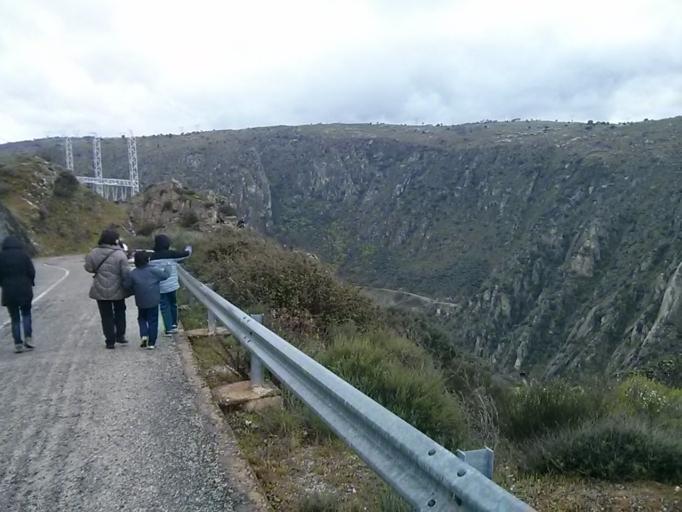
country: ES
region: Castille and Leon
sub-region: Provincia de Salamanca
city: Mieza
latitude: 41.2122
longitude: -6.6804
